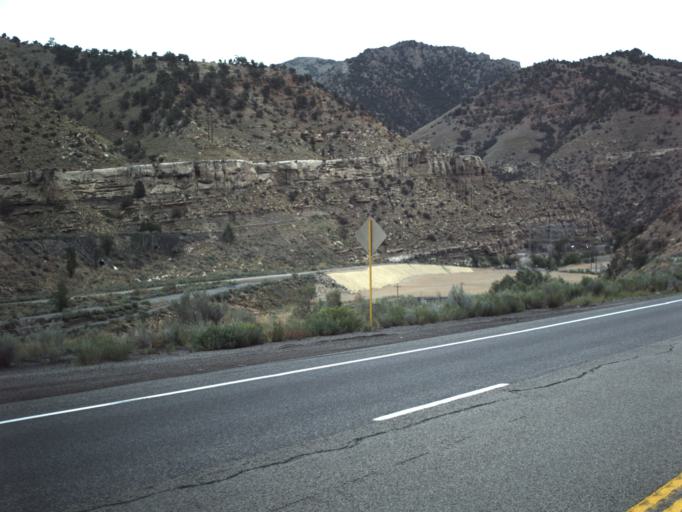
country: US
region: Utah
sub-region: Carbon County
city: Helper
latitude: 39.7301
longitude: -110.8694
